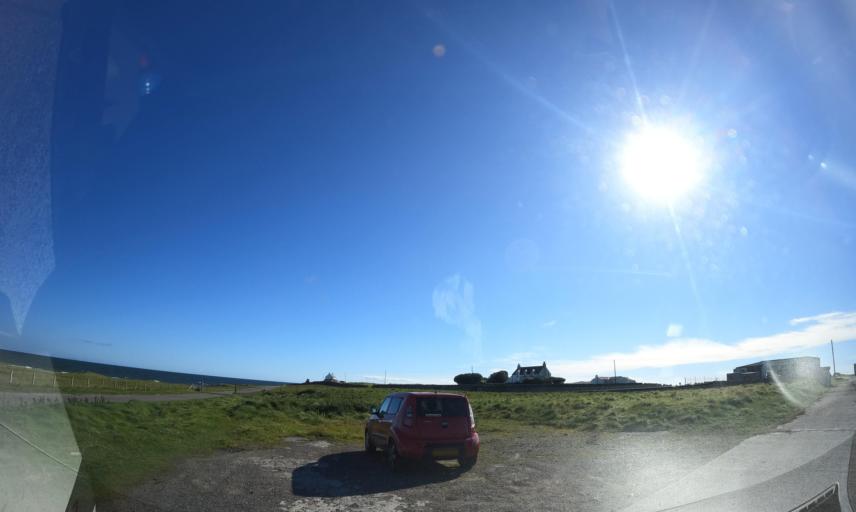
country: GB
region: Scotland
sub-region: Eilean Siar
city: Barra
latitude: 56.4887
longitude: -6.8797
